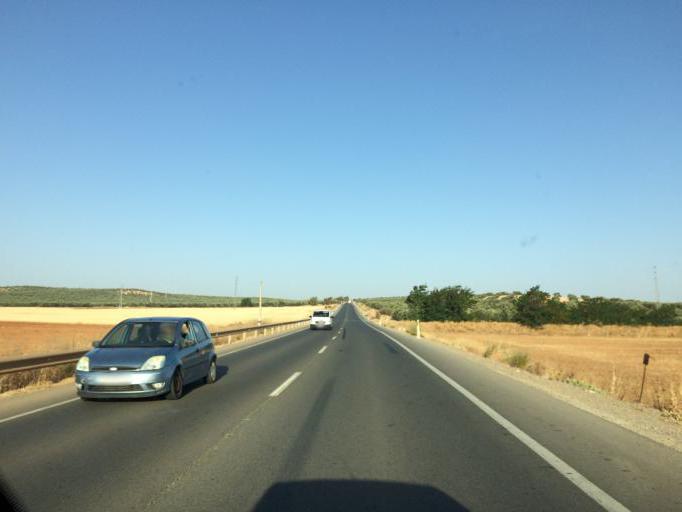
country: ES
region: Andalusia
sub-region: Provincia de Malaga
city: Humilladero
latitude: 37.0530
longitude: -4.7644
